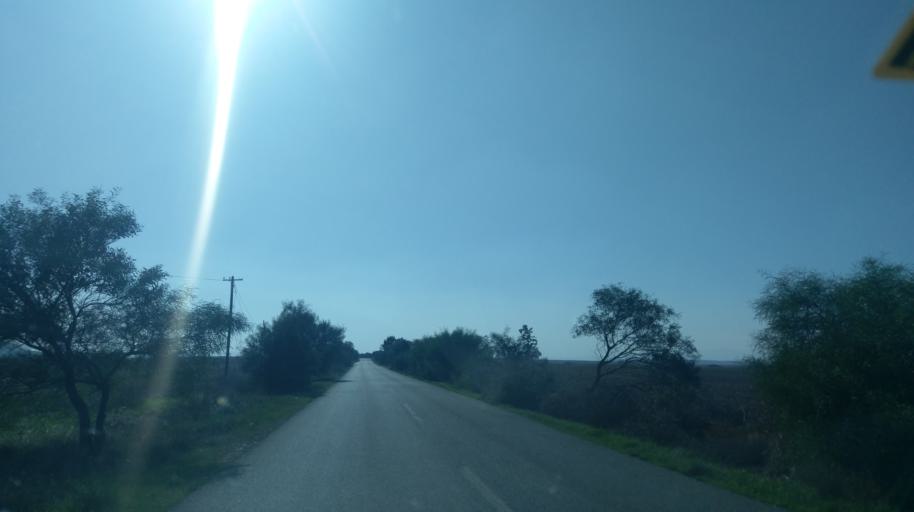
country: CY
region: Larnaka
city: Athienou
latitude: 35.1176
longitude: 33.5018
